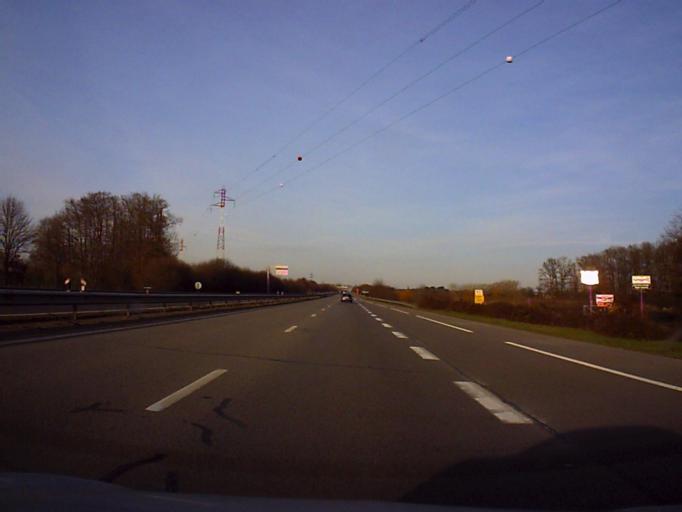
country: FR
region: Brittany
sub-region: Departement d'Ille-et-Vilaine
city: Le Rheu
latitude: 48.0812
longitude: -1.7907
